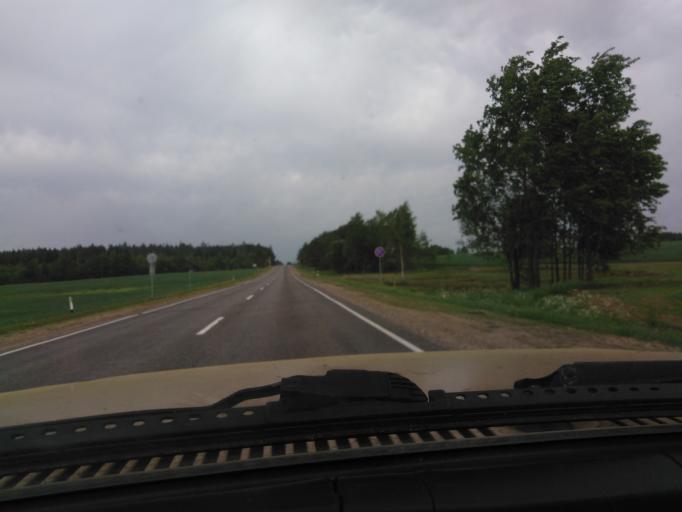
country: BY
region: Mogilev
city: Kamyennyya Lavy
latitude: 54.0417
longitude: 30.3248
